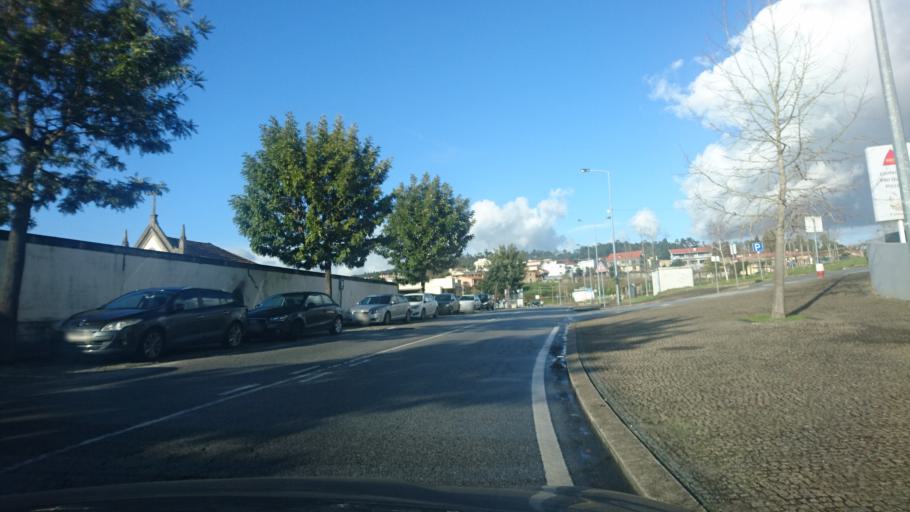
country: PT
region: Porto
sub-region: Paredes
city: Recarei
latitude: 41.1462
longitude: -8.3911
